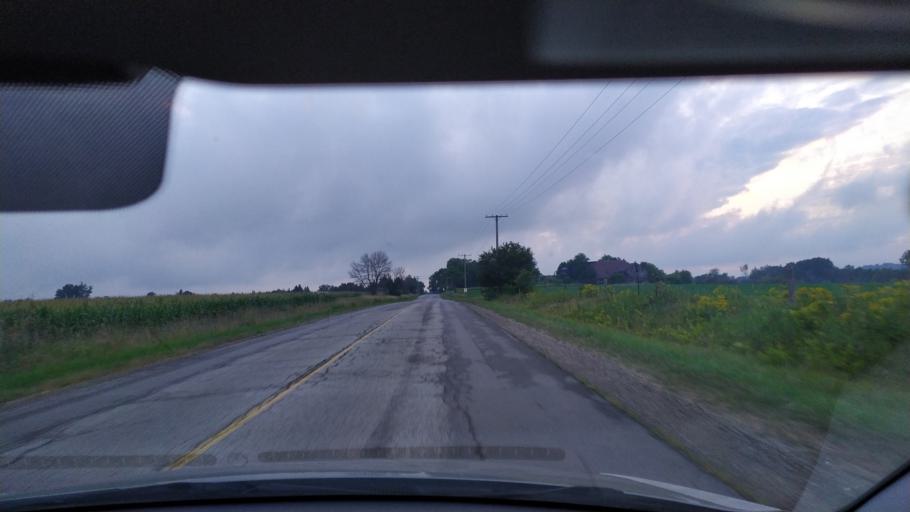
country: CA
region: Ontario
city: Kitchener
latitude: 43.3573
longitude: -80.6519
